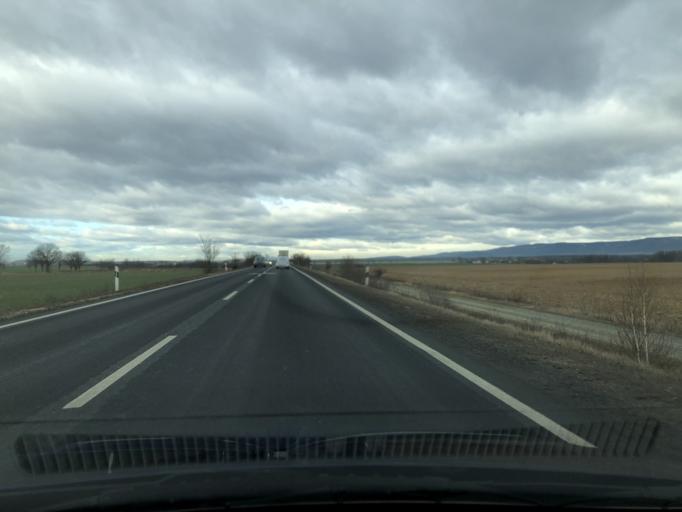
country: HU
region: Vas
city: Gencsapati
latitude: 47.2495
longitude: 16.5592
